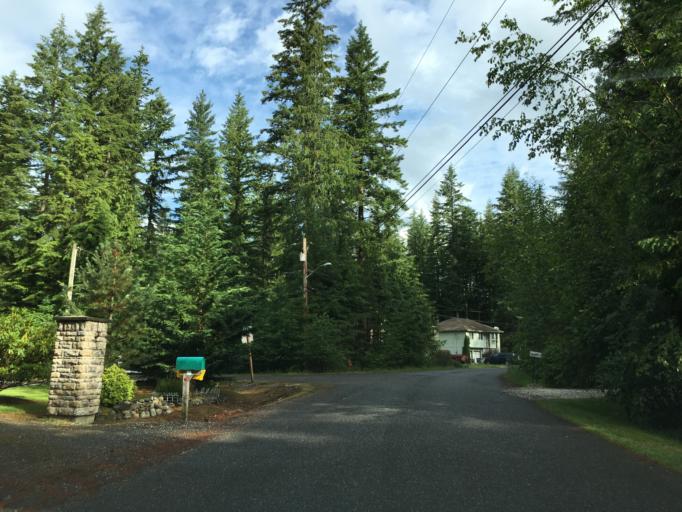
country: US
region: Washington
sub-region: Whatcom County
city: Peaceful Valley
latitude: 48.9400
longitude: -122.1462
